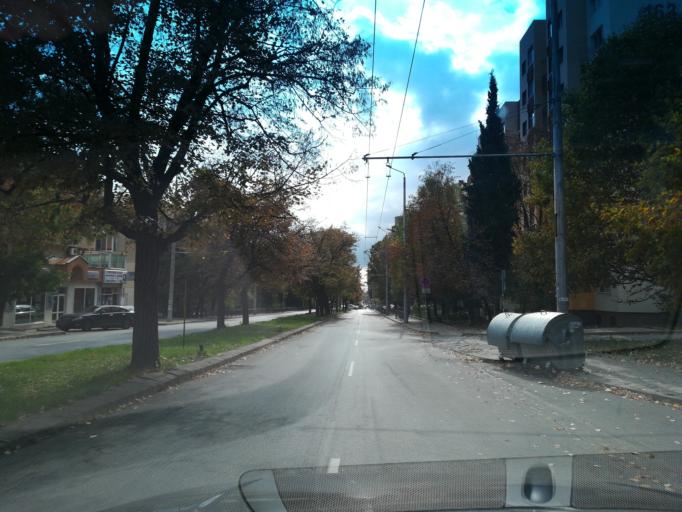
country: BG
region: Stara Zagora
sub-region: Obshtina Stara Zagora
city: Stara Zagora
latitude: 42.4358
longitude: 25.6314
